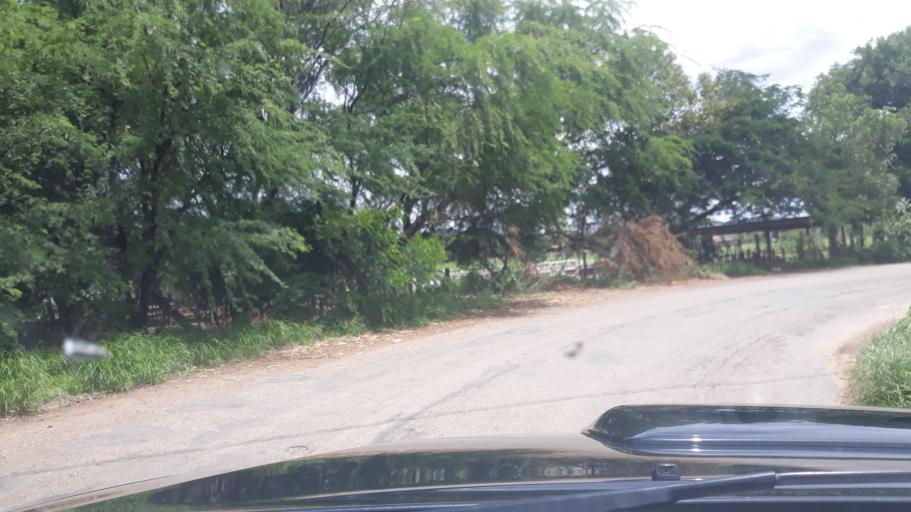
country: BR
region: Bahia
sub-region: Guanambi
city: Guanambi
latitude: -14.2922
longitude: -42.6964
